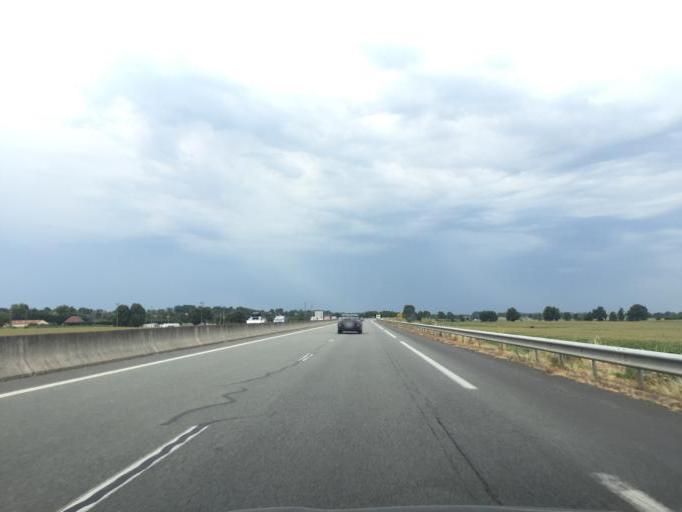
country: FR
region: Auvergne
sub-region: Departement de l'Allier
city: Toulon-sur-Allier
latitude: 46.5181
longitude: 3.3530
